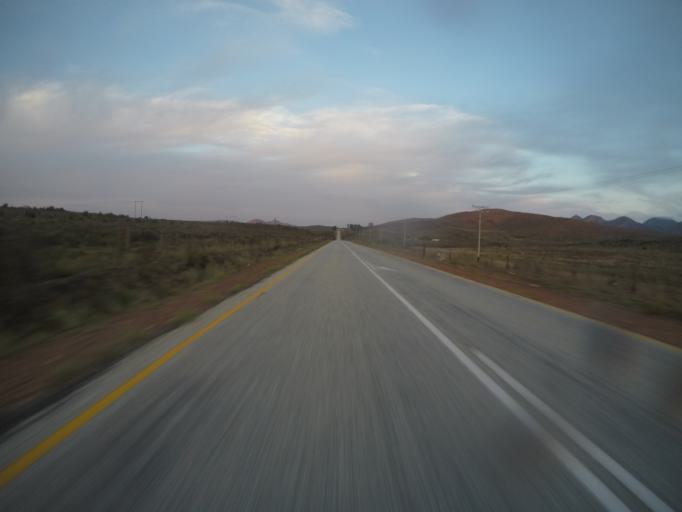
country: ZA
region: Western Cape
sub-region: Eden District Municipality
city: Plettenberg Bay
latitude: -33.7388
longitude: 23.4253
